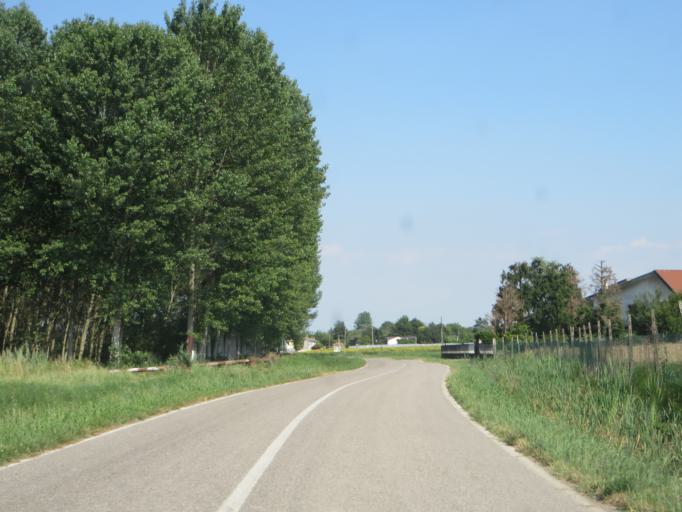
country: IT
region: Veneto
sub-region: Provincia di Verona
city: Angiari
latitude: 45.2249
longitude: 11.2647
